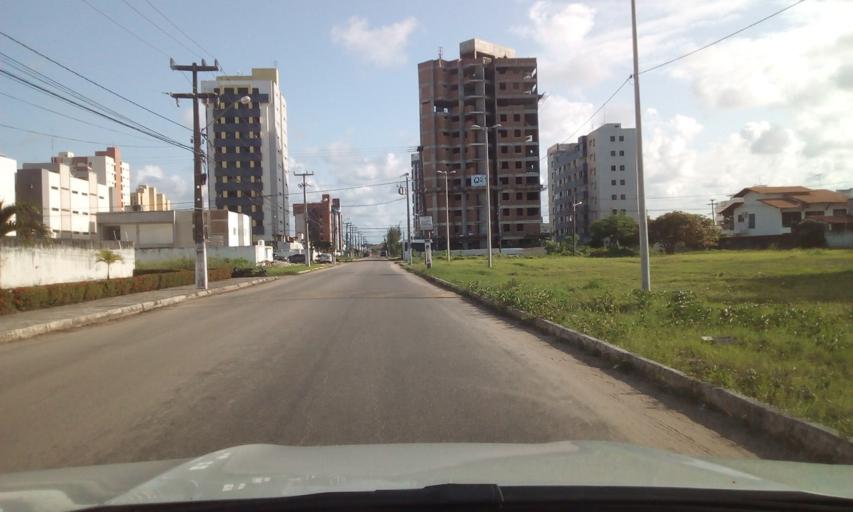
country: BR
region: Paraiba
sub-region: Cabedelo
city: Cabedelo
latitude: -7.0449
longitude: -34.8452
